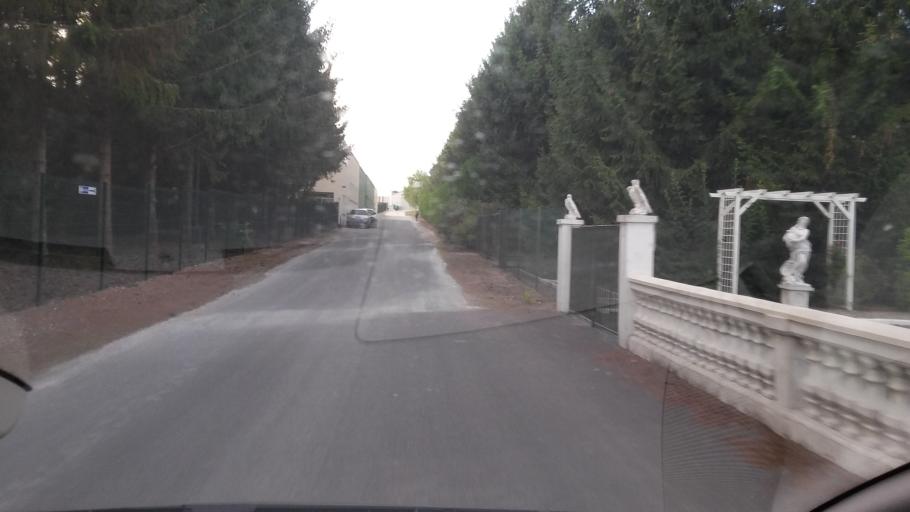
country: FR
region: Champagne-Ardenne
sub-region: Departement de la Marne
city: Fere-Champenoise
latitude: 48.7577
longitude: 3.9933
